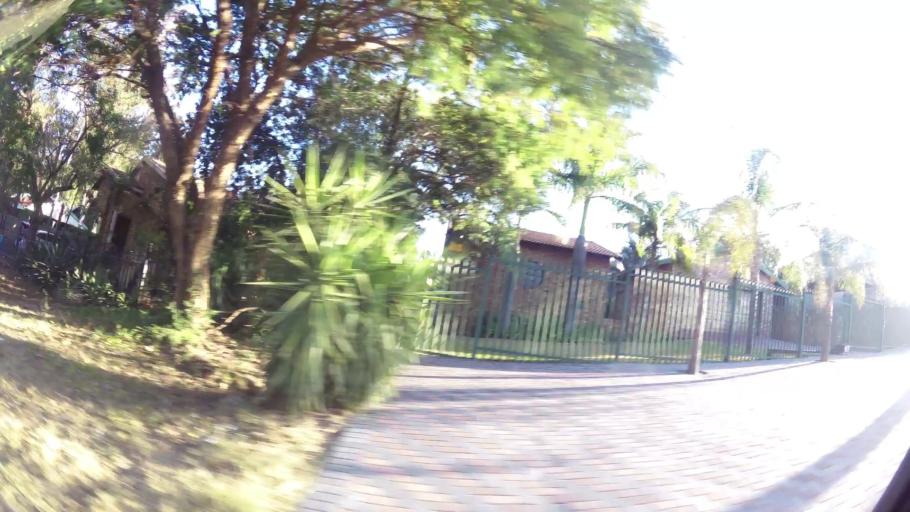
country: ZA
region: North-West
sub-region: Bojanala Platinum District Municipality
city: Rustenburg
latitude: -25.6801
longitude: 27.2024
